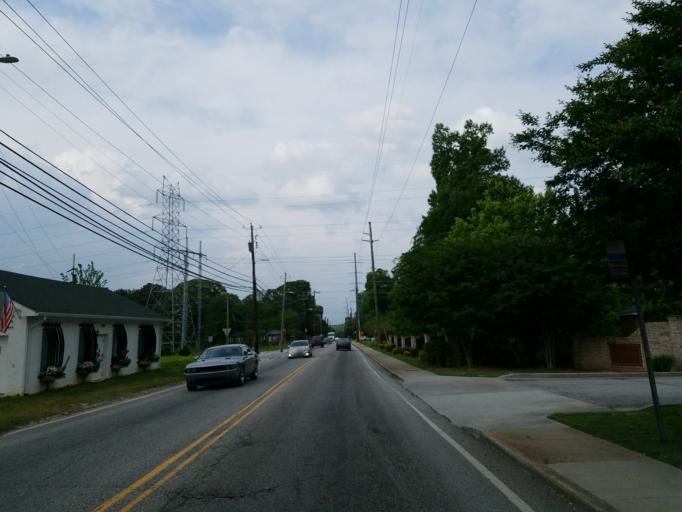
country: US
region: Georgia
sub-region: Cobb County
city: Vinings
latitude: 33.8143
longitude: -84.4679
